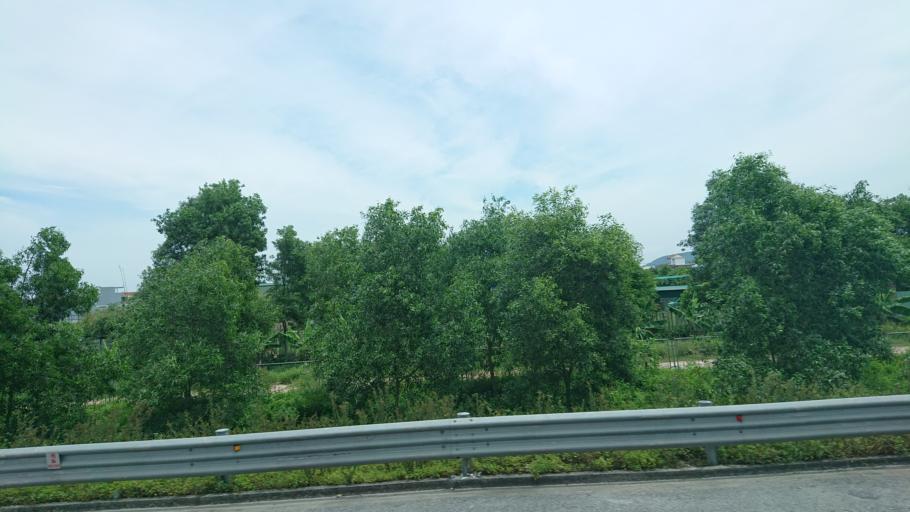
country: VN
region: Hai Phong
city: Nui Doi
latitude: 20.7707
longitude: 106.6146
